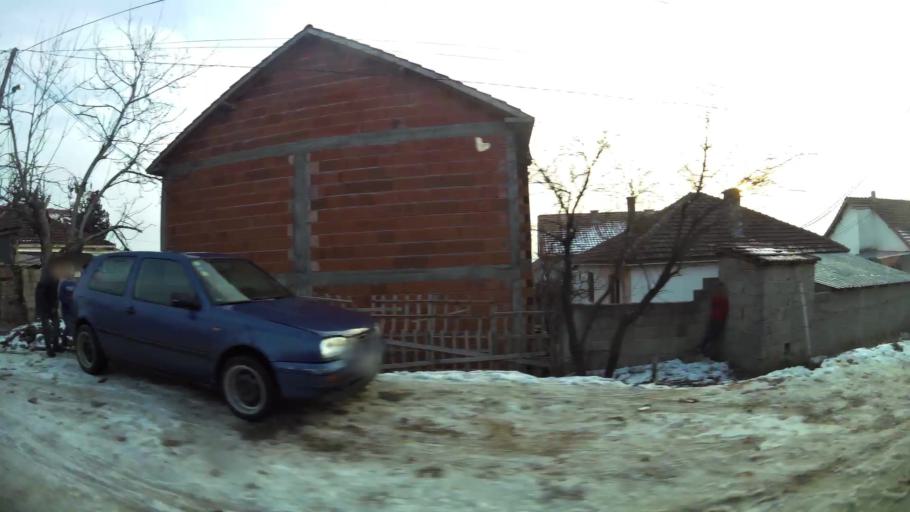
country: MK
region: Aracinovo
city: Arachinovo
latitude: 42.0268
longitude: 21.5572
